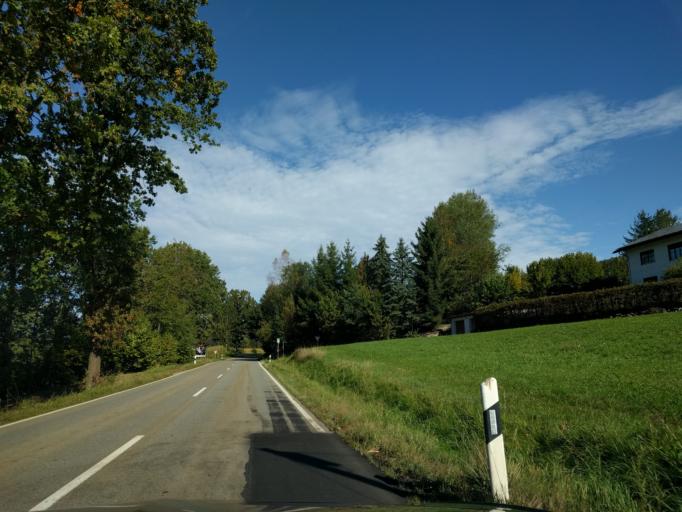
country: DE
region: Bavaria
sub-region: Lower Bavaria
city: Viechtach
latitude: 49.0997
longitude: 12.8867
